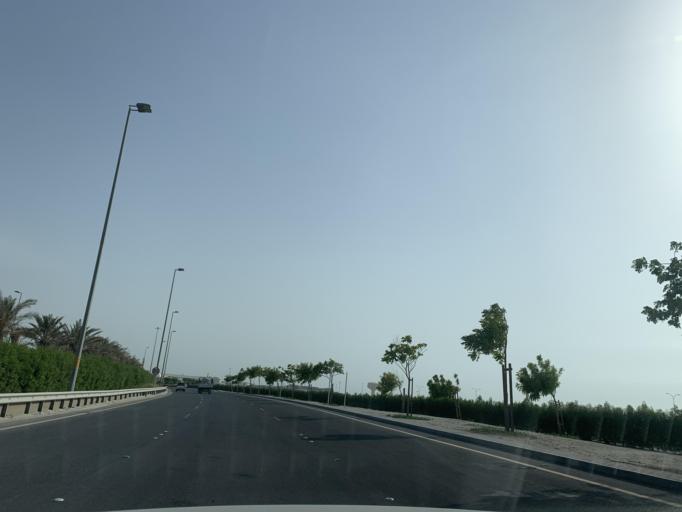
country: BH
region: Muharraq
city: Al Muharraq
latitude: 26.3110
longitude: 50.6410
